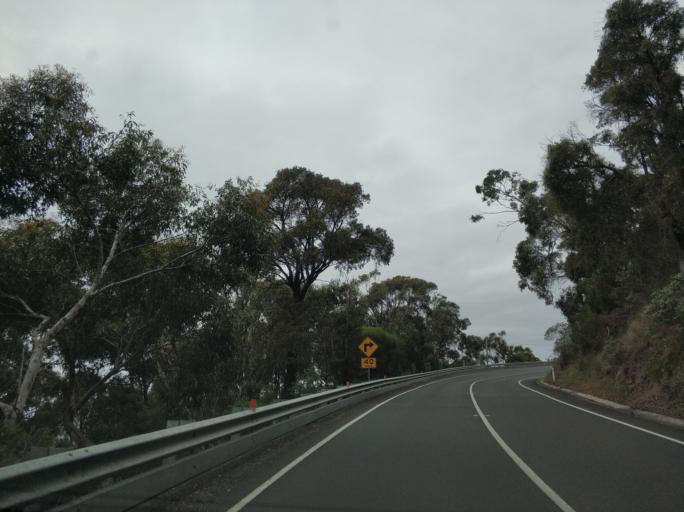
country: AU
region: Victoria
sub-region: Surf Coast
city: Anglesea
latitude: -38.4855
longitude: 144.0288
